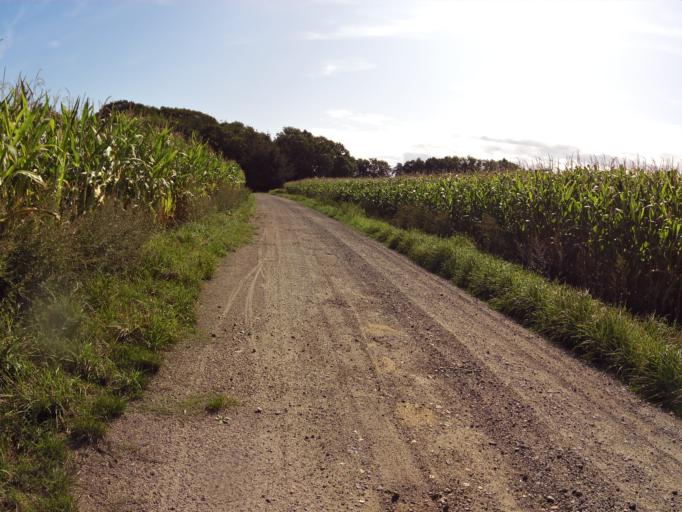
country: DE
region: Lower Saxony
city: Sandbostel
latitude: 53.3999
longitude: 9.1211
